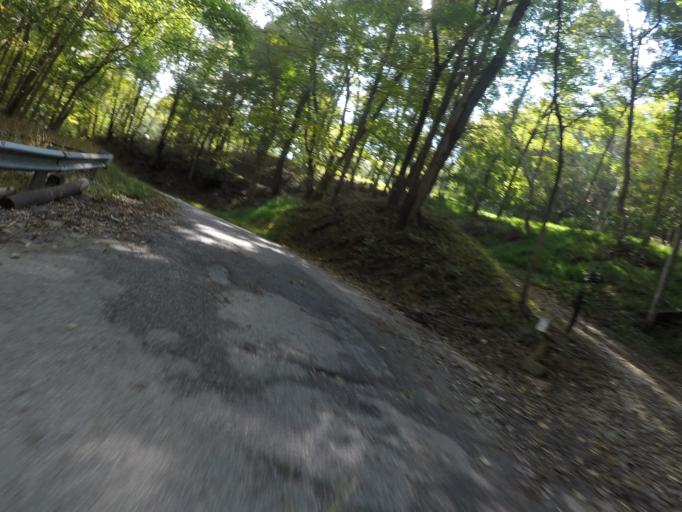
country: US
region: West Virginia
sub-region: Wayne County
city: Lavalette
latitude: 38.3676
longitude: -82.4785
